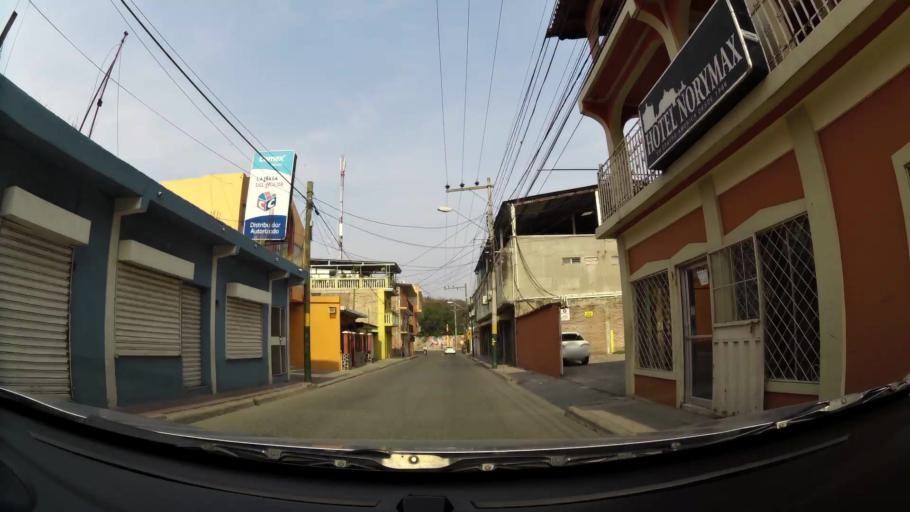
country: HN
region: Comayagua
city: Comayagua
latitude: 14.4561
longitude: -87.6431
